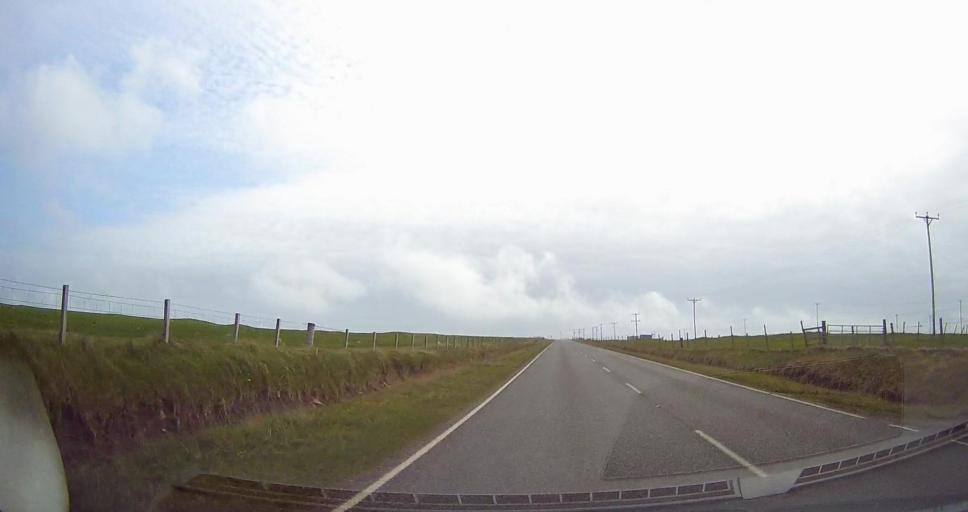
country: GB
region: Scotland
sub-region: Shetland Islands
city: Sandwick
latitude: 59.9020
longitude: -1.3030
